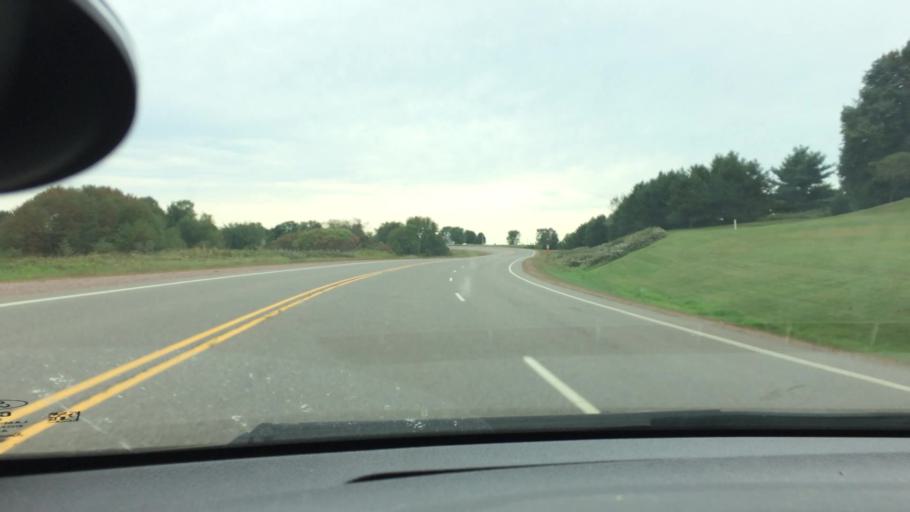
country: US
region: Wisconsin
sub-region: Clark County
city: Neillsville
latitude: 44.5562
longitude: -90.6401
